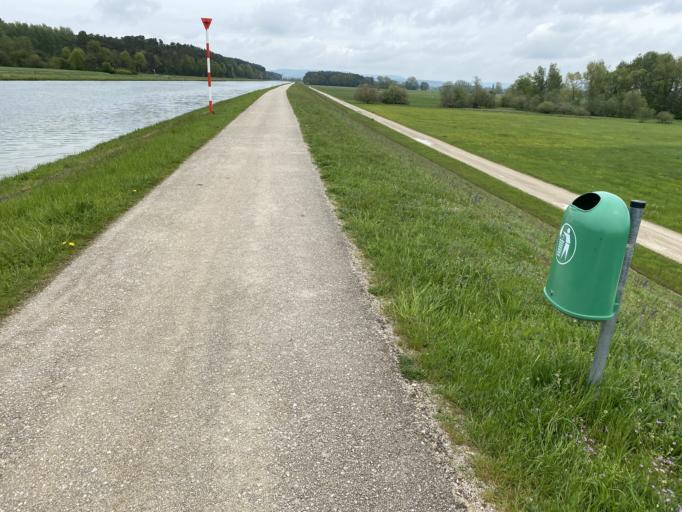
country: DE
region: Bavaria
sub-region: Regierungsbezirk Mittelfranken
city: Baiersdorf
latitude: 49.6657
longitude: 11.0197
